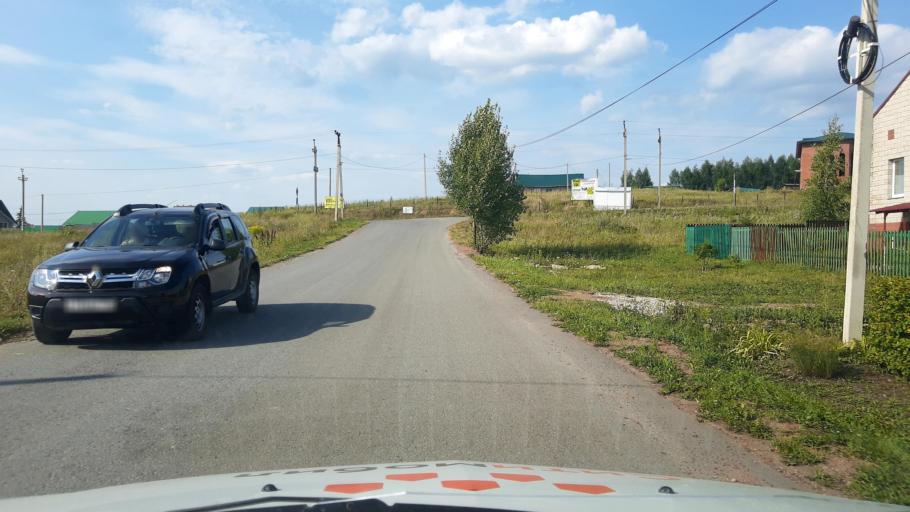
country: RU
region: Bashkortostan
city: Kabakovo
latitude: 54.6661
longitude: 56.2139
